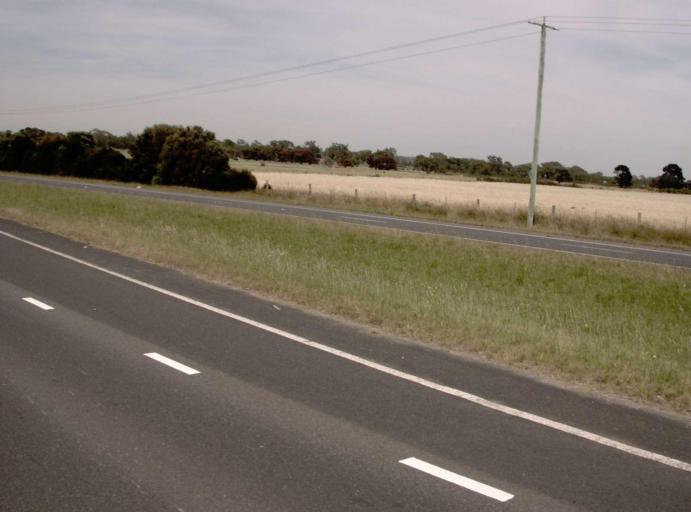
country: AU
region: Victoria
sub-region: Casey
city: Lynbrook
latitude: -38.0691
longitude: 145.2413
